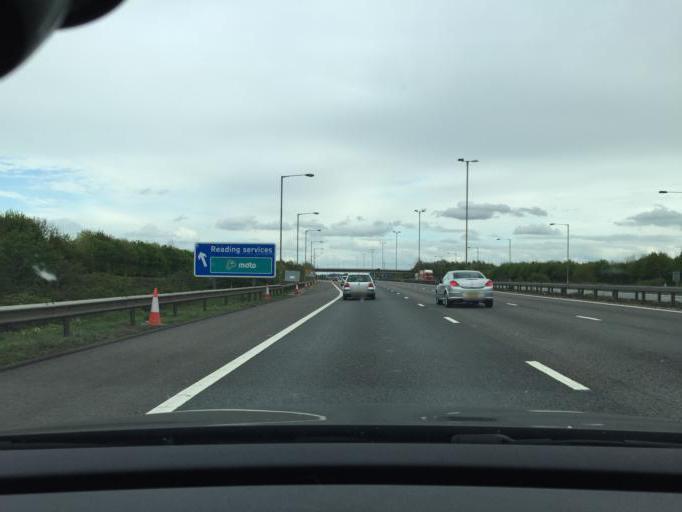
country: GB
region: England
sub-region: West Berkshire
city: Calcot
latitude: 51.4252
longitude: -1.0365
